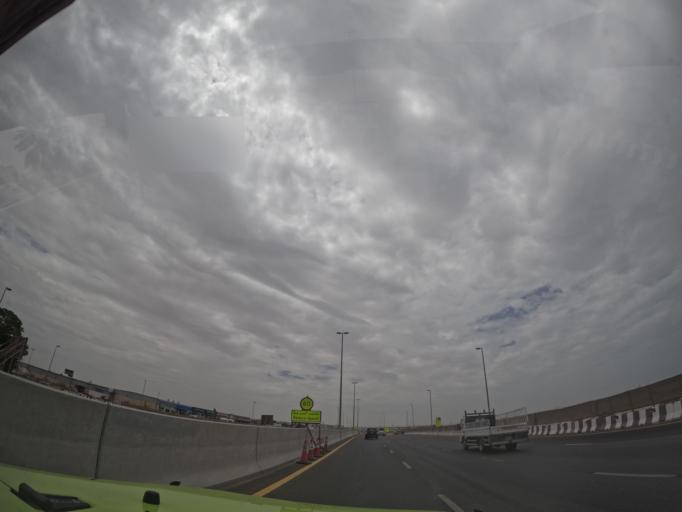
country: AE
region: Ash Shariqah
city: Sharjah
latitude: 25.1943
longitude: 55.3725
